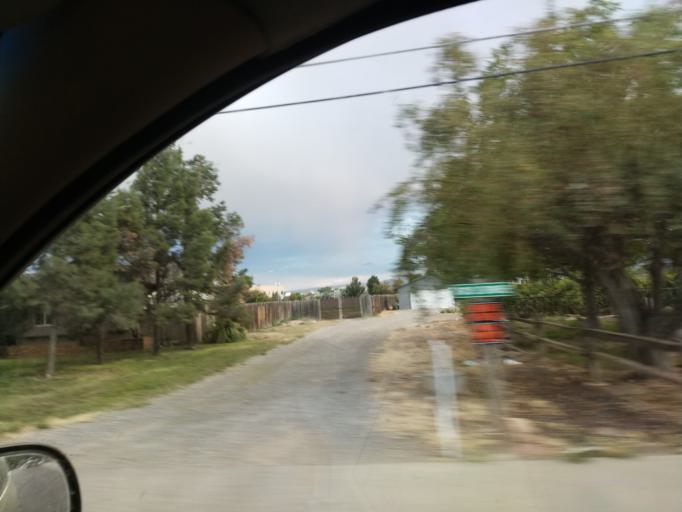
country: US
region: Colorado
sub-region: Mesa County
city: Fruitvale
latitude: 39.0810
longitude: -108.5214
